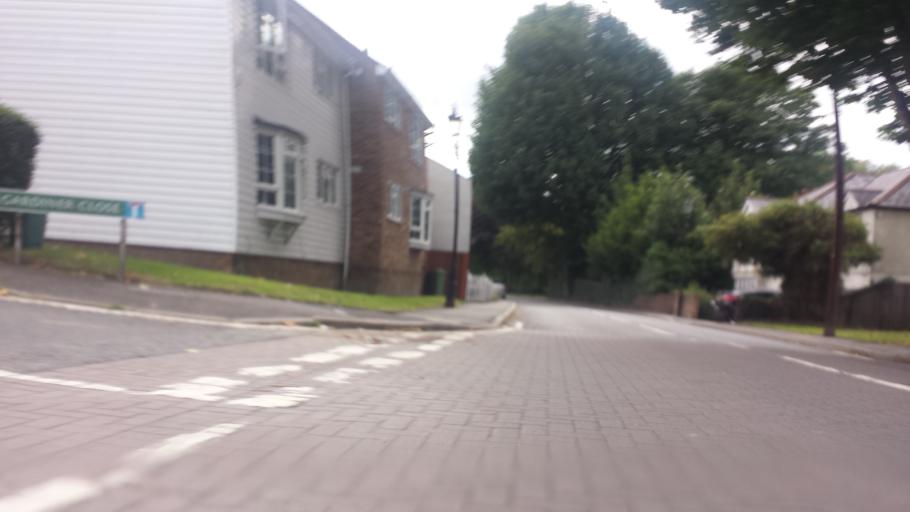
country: GB
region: England
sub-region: Greater London
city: Sidcup
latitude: 51.4028
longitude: 0.1180
